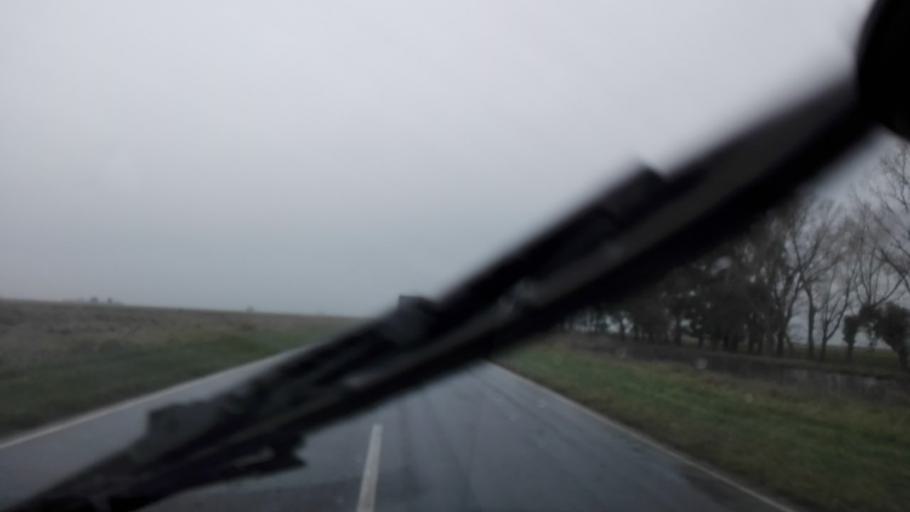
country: AR
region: Buenos Aires
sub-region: Partido de Tandil
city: Tandil
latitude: -37.0774
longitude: -58.9994
